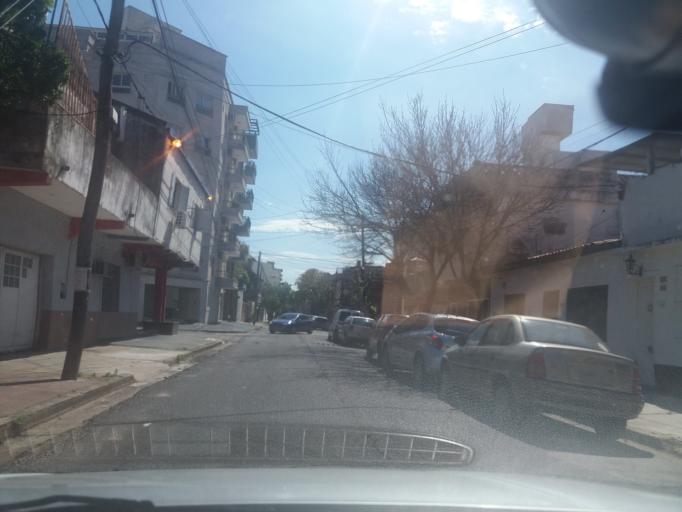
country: AR
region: Corrientes
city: Corrientes
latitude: -27.4694
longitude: -58.8457
